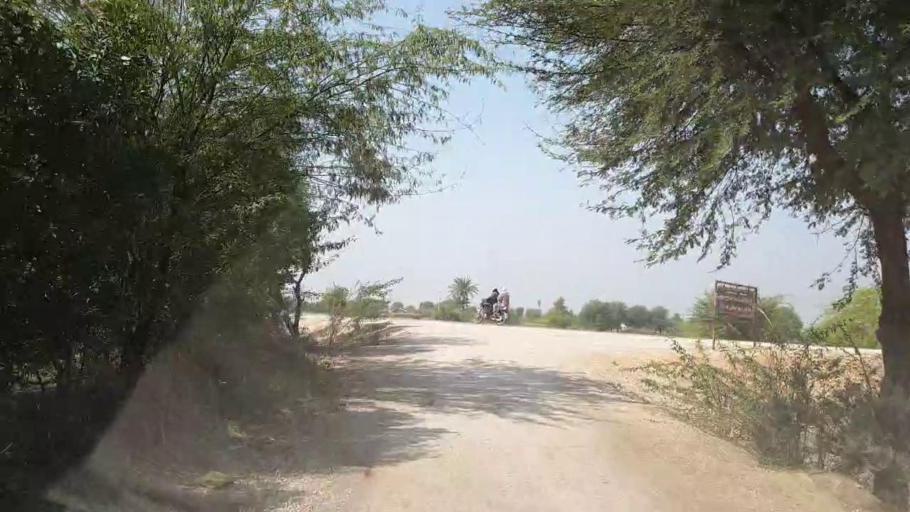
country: PK
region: Sindh
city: Mirpur Khas
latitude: 25.6236
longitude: 69.0898
